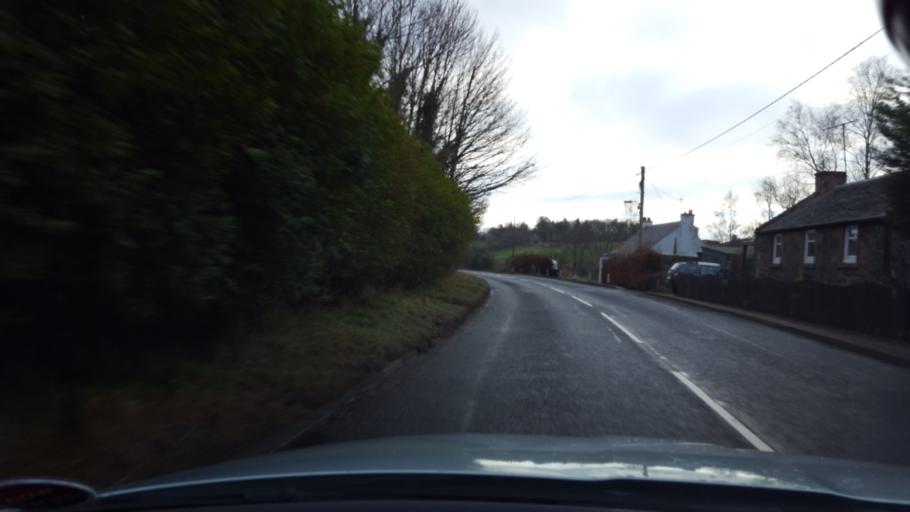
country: GB
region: Scotland
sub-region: Perth and Kinross
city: Milnathort
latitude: 56.2751
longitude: -3.3973
